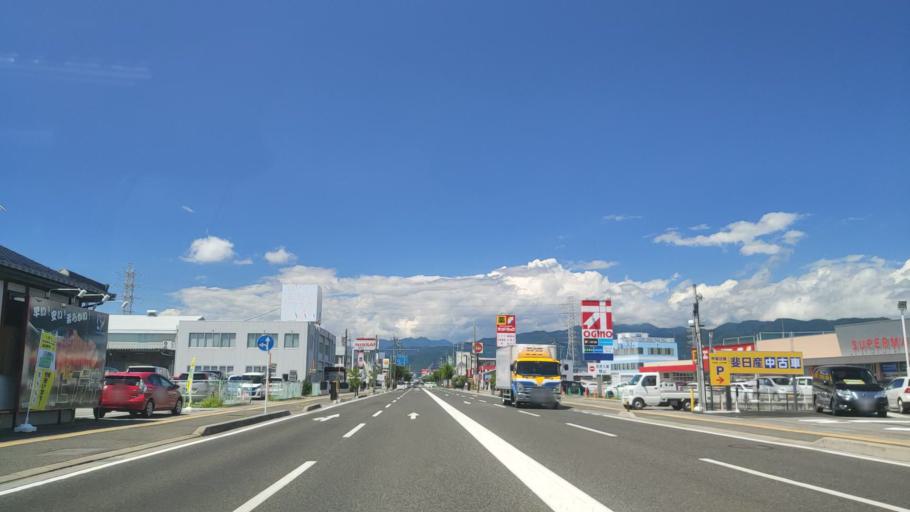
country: JP
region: Yamanashi
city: Kofu-shi
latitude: 35.6242
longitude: 138.5720
